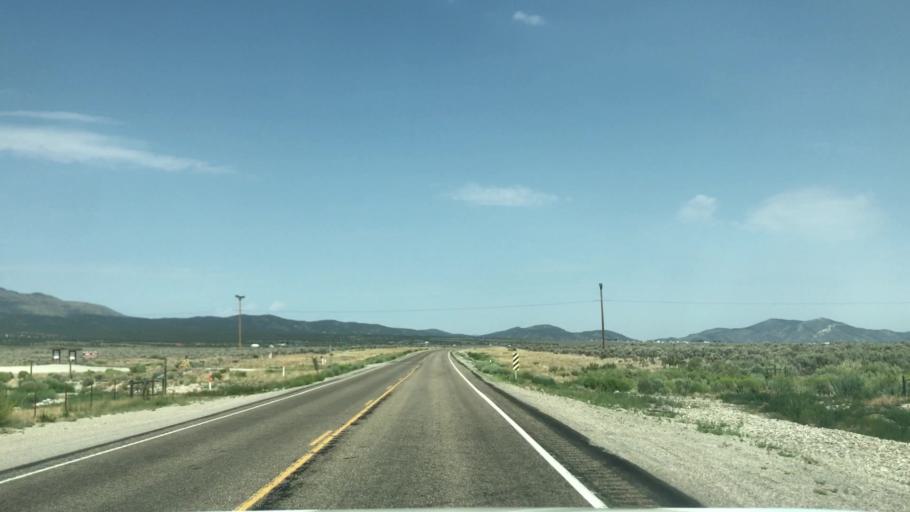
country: US
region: Nevada
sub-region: White Pine County
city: Ely
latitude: 39.1663
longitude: -114.8138
